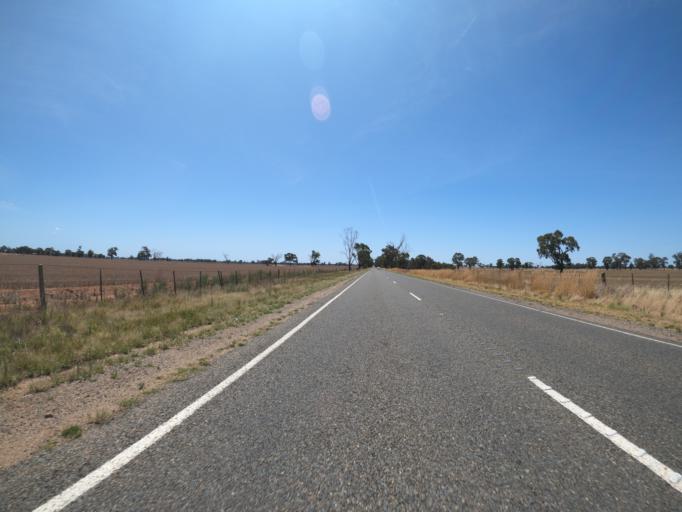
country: AU
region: Victoria
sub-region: Moira
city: Yarrawonga
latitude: -36.0730
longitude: 145.9954
